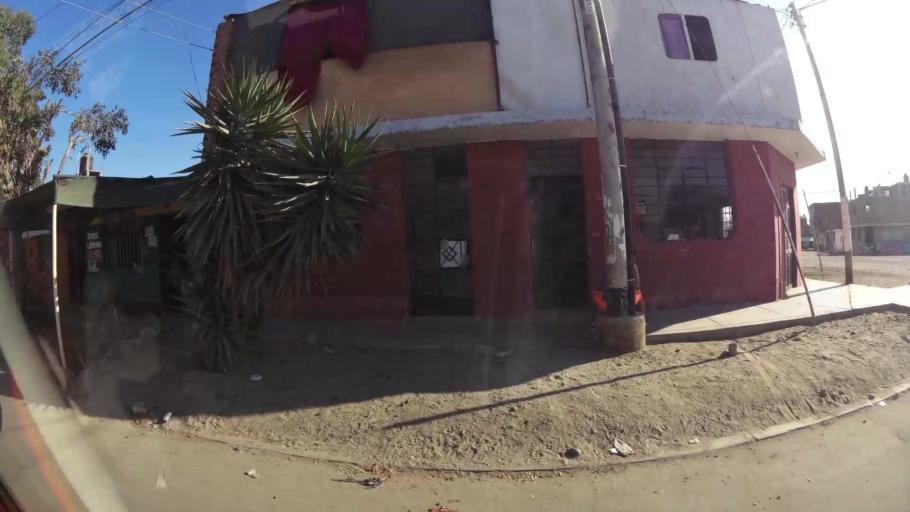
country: PE
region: Ica
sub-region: Provincia de Ica
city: La Tinguina
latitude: -14.0427
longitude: -75.7027
